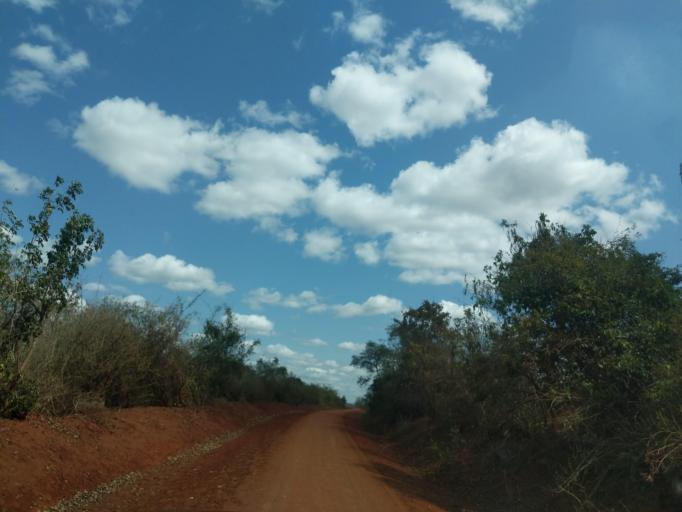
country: TZ
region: Tanga
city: Chanika
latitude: -5.5167
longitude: 38.3540
